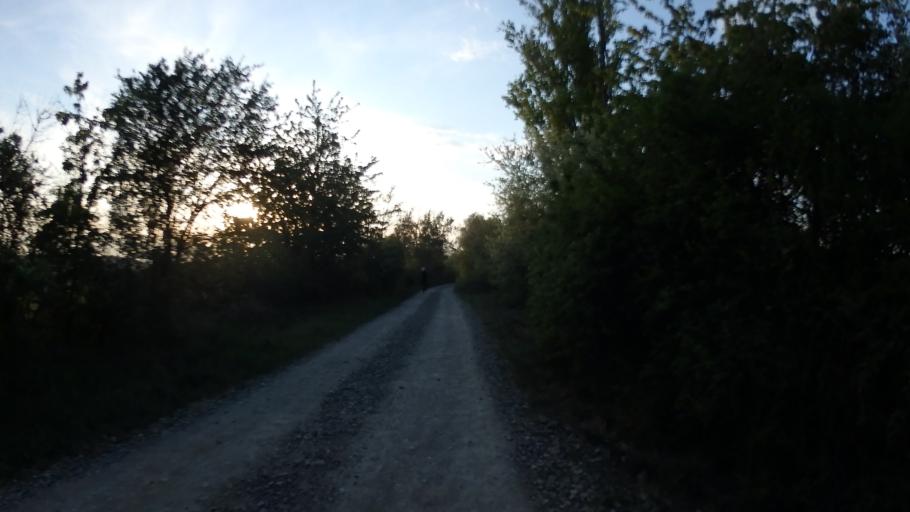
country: CZ
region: South Moravian
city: Ostopovice
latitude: 49.1470
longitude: 16.5521
